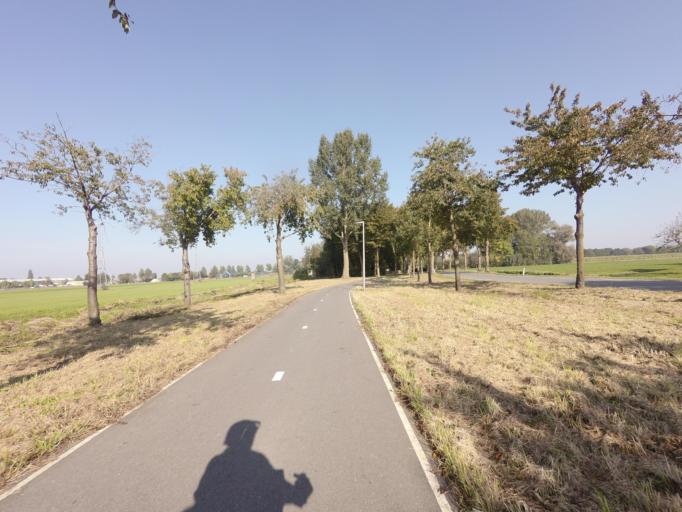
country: NL
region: Utrecht
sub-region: Gemeente Vianen
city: Vianen
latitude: 51.9542
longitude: 5.1485
